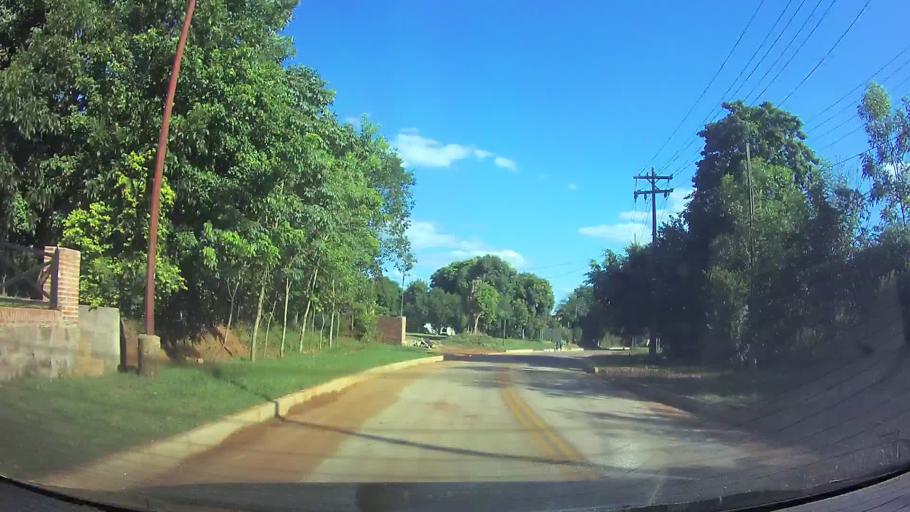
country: PY
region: Cordillera
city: Caacupe
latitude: -25.3727
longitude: -57.1382
